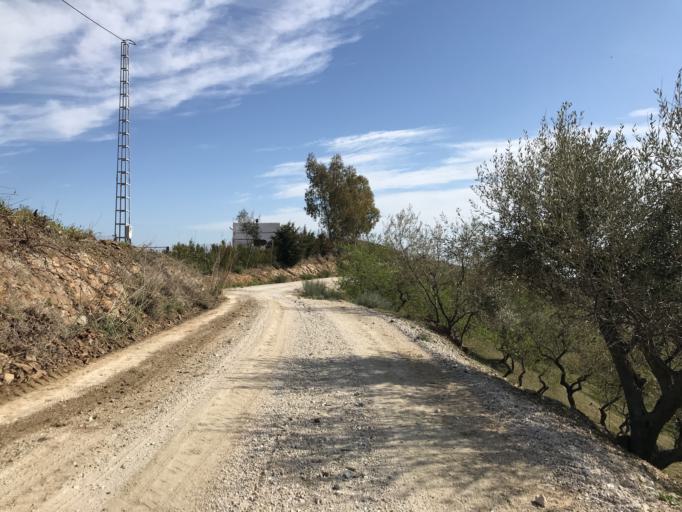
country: ES
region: Andalusia
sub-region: Provincia de Malaga
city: Almachar
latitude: 36.7802
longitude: -4.2180
